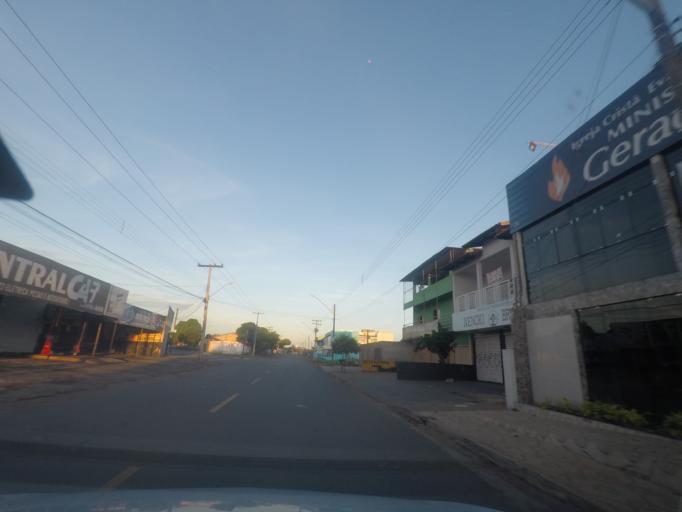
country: BR
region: Goias
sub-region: Goiania
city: Goiania
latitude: -16.6887
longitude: -49.3464
